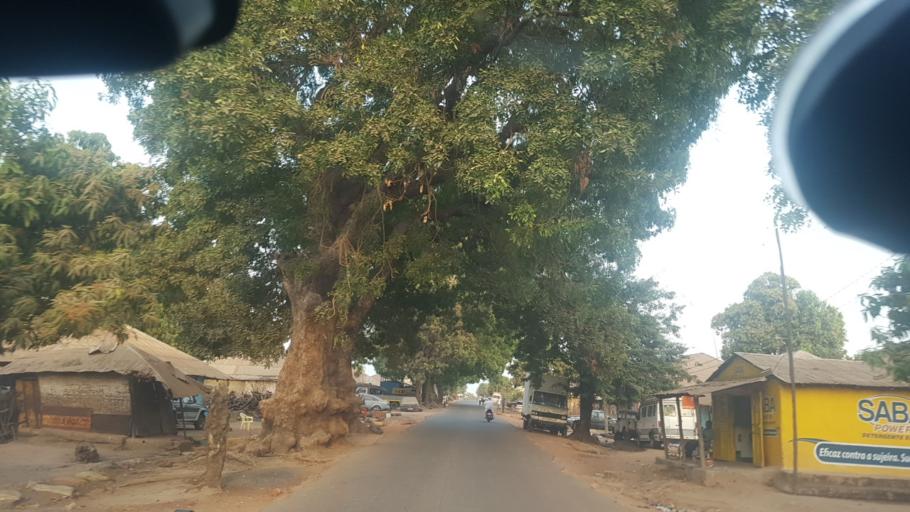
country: SN
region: Ziguinchor
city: Adeane
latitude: 12.4099
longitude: -15.8040
